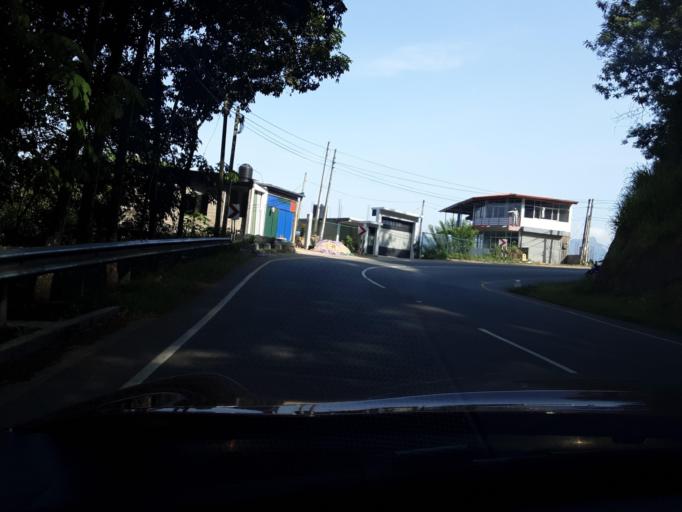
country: LK
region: Uva
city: Badulla
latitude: 6.9848
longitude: 81.0760
